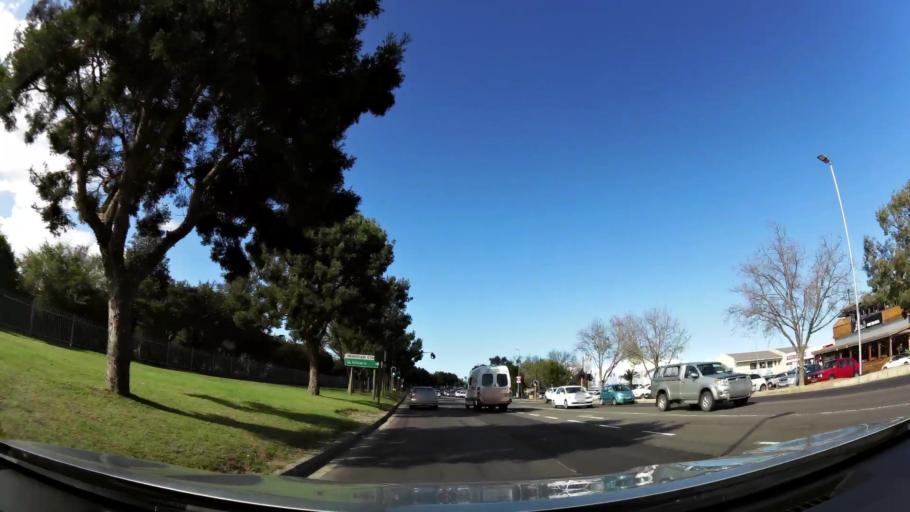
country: ZA
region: Western Cape
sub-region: Eden District Municipality
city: George
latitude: -33.9606
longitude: 22.4697
